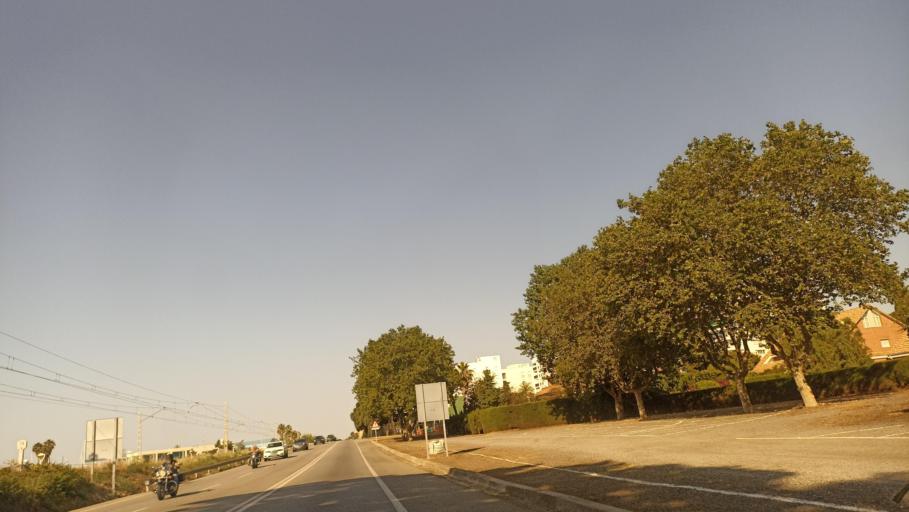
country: ES
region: Catalonia
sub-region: Provincia de Barcelona
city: Caldes d'Estrac
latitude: 41.5618
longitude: 2.5103
